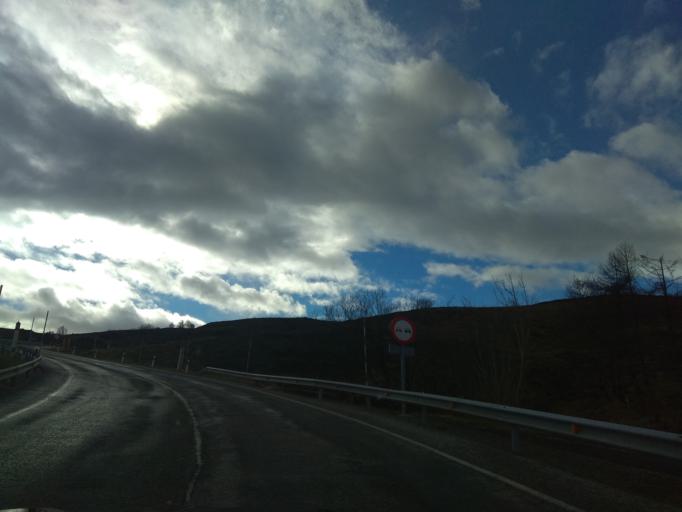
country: ES
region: Cantabria
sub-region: Provincia de Cantabria
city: San Pedro del Romeral
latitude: 43.0622
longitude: -3.8865
